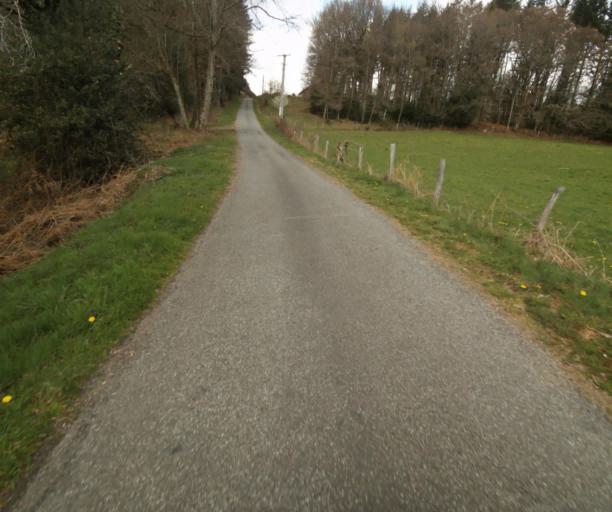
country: FR
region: Limousin
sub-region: Departement de la Correze
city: Correze
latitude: 45.3503
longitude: 1.9352
